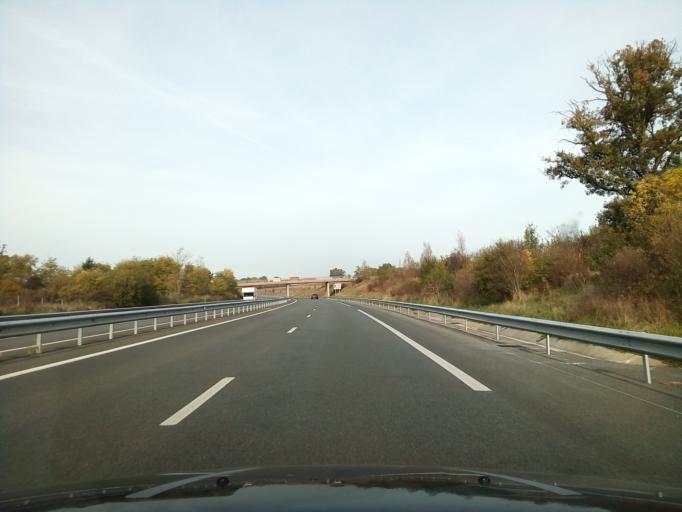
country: FR
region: Rhone-Alpes
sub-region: Departement de la Loire
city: La Pacaudiere
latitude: 46.1799
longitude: 3.8777
